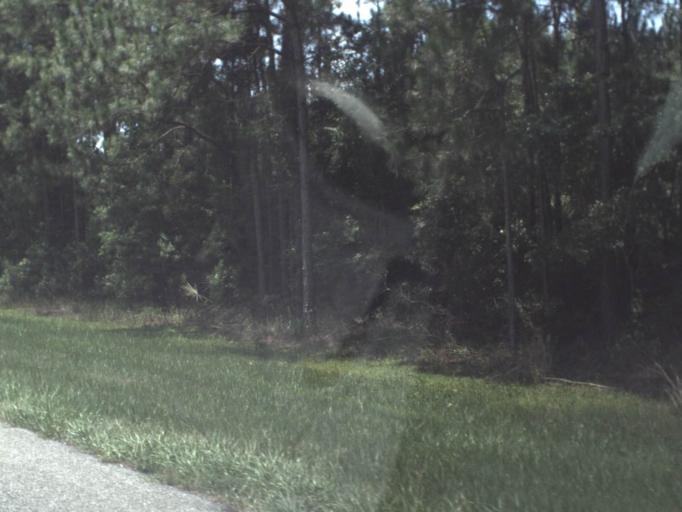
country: US
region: Florida
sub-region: Saint Johns County
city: Butler Beach
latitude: 29.7144
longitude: -81.3025
